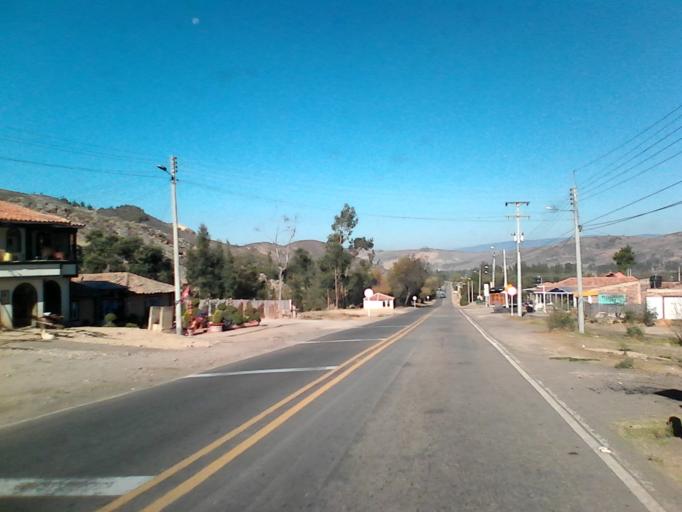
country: CO
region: Boyaca
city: Cucaita
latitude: 5.5393
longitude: -73.4513
